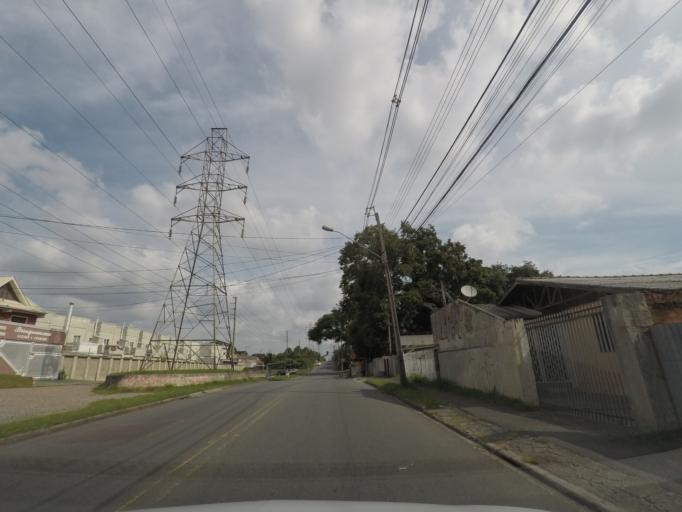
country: BR
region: Parana
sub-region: Pinhais
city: Pinhais
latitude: -25.4801
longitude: -49.2112
